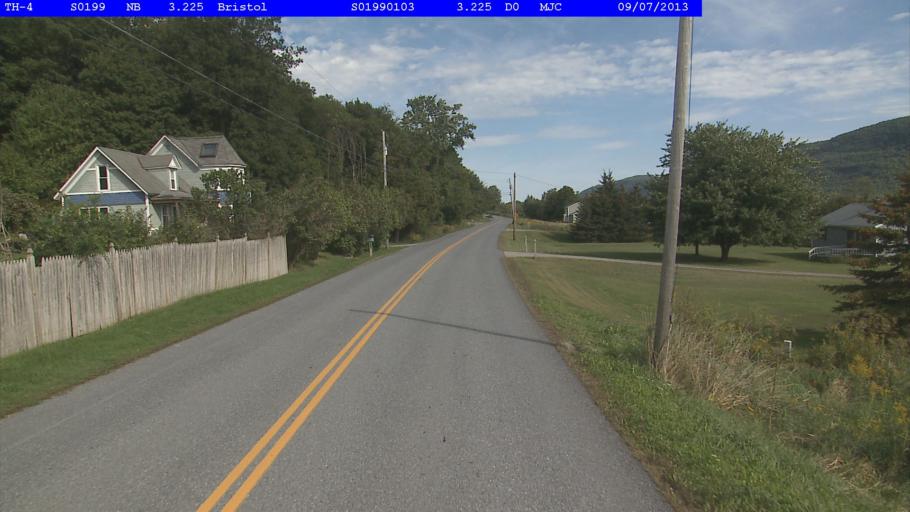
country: US
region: Vermont
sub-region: Addison County
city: Bristol
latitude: 44.1747
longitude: -73.1022
